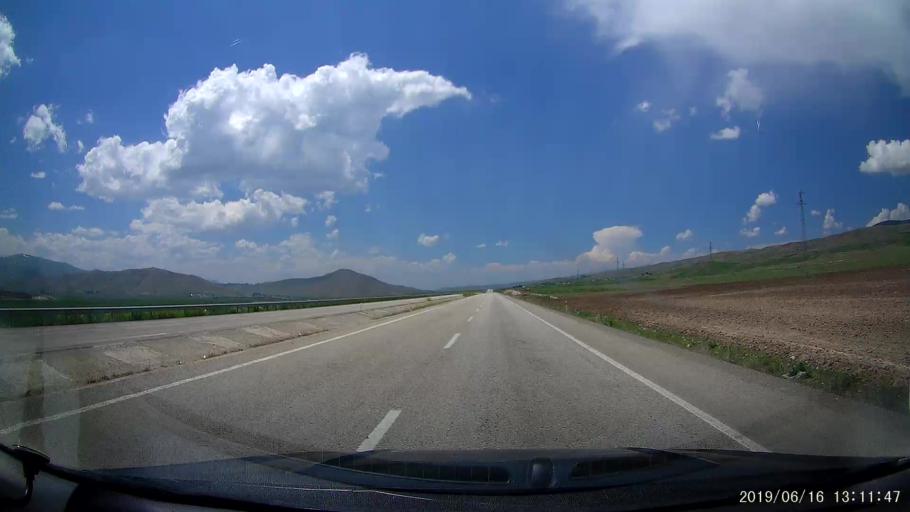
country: TR
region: Agri
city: Diyadin
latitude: 39.5937
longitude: 43.5978
